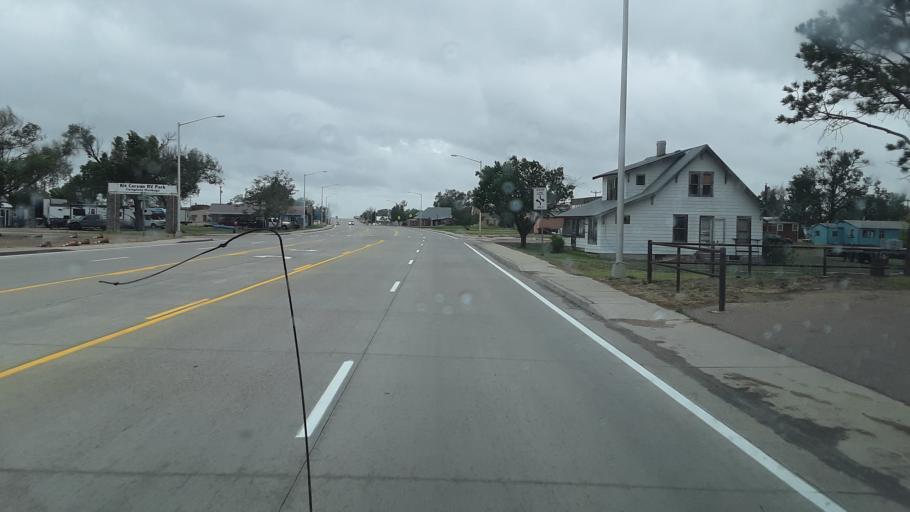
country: US
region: Colorado
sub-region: Kiowa County
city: Eads
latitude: 38.7643
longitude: -102.7887
